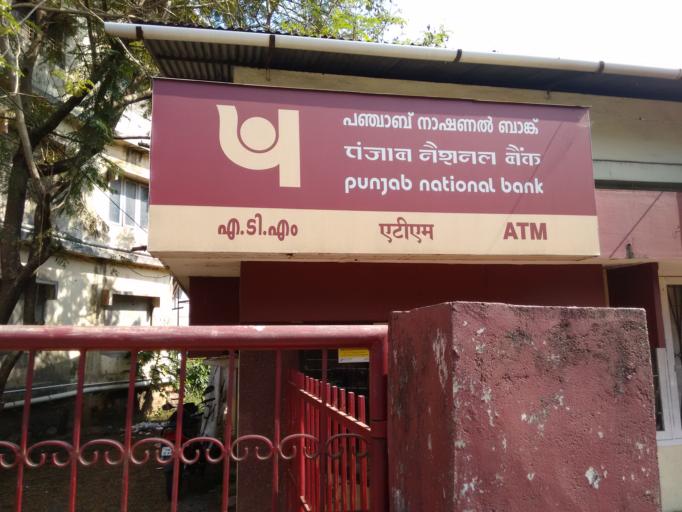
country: IN
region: Kerala
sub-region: Kozhikode
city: Badagara
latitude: 11.5971
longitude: 75.5887
